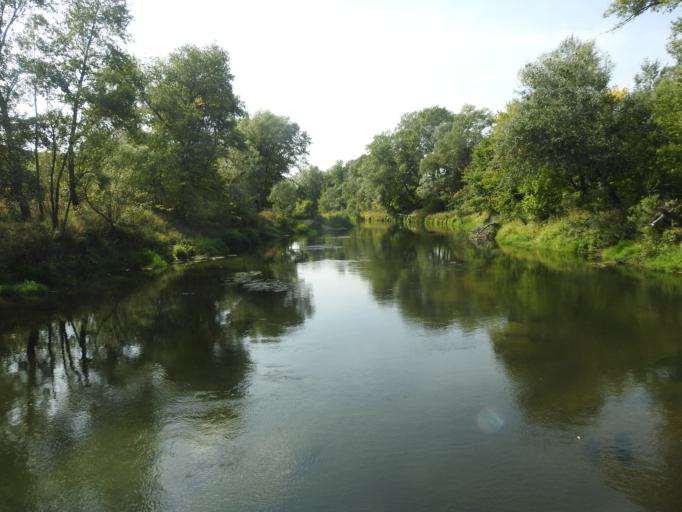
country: RU
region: Saratov
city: Lysyye Gory
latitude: 51.2940
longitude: 44.9992
